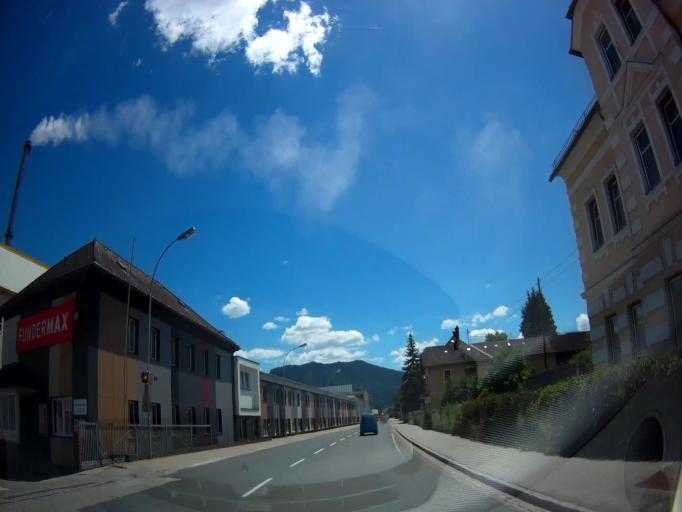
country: AT
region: Carinthia
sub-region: Politischer Bezirk Sankt Veit an der Glan
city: Sankt Veit an der Glan
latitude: 46.7576
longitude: 14.3768
